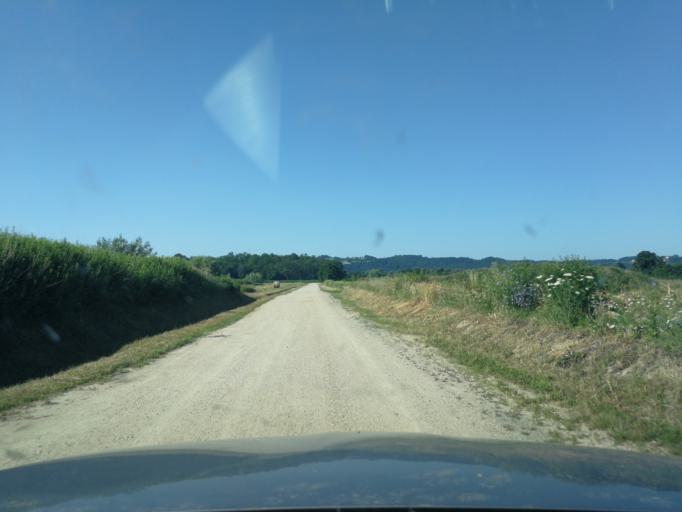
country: AT
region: Burgenland
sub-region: Politischer Bezirk Jennersdorf
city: Konigsdorf
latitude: 47.0125
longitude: 16.1597
